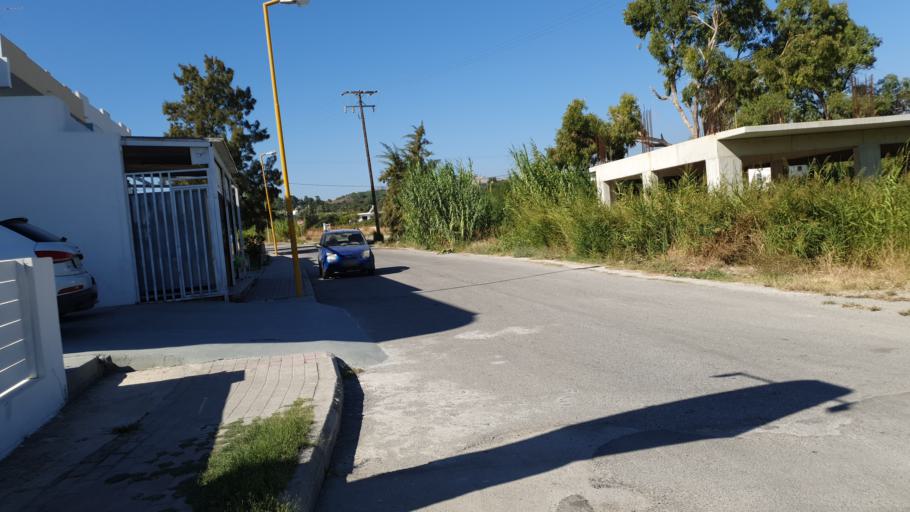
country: GR
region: South Aegean
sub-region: Nomos Dodekanisou
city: Faliraki
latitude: 36.3322
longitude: 28.2078
